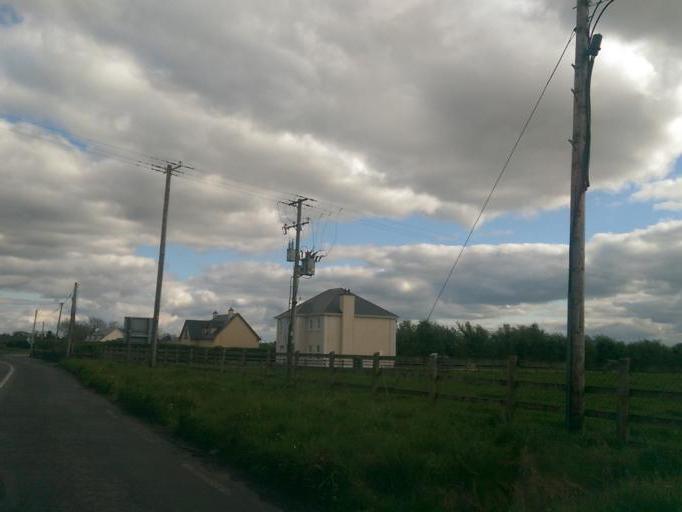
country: IE
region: Connaught
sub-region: County Galway
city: Ballinasloe
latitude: 53.4129
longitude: -8.3440
